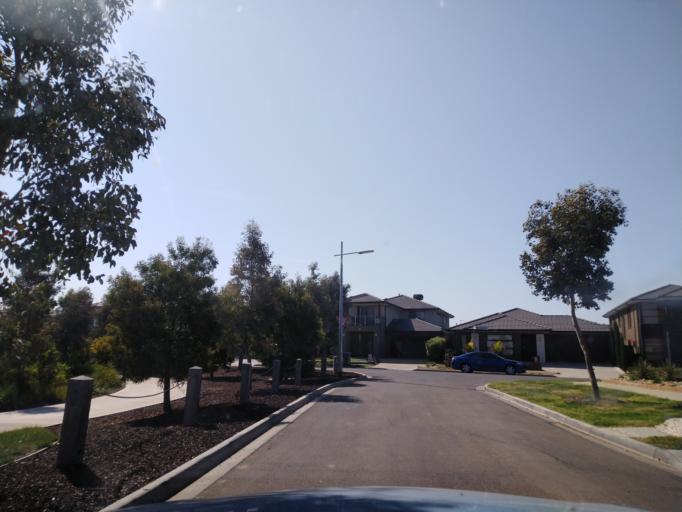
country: AU
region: Victoria
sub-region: Wyndham
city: Williams Landing
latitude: -37.8466
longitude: 144.7377
